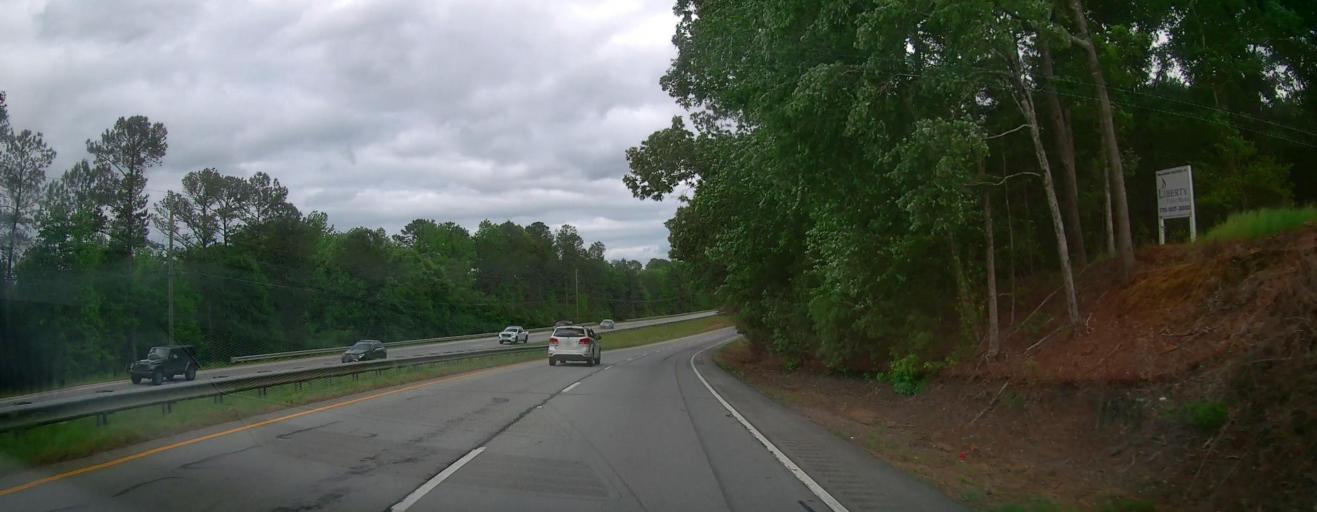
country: US
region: Georgia
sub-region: Walton County
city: Monroe
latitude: 33.8068
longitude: -83.7713
